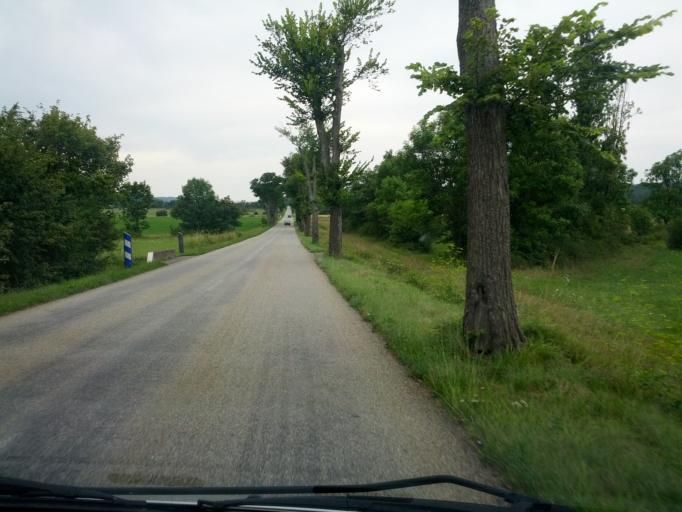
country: FR
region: Languedoc-Roussillon
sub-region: Departement de l'Aude
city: Quillan
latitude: 42.8853
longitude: 2.1319
